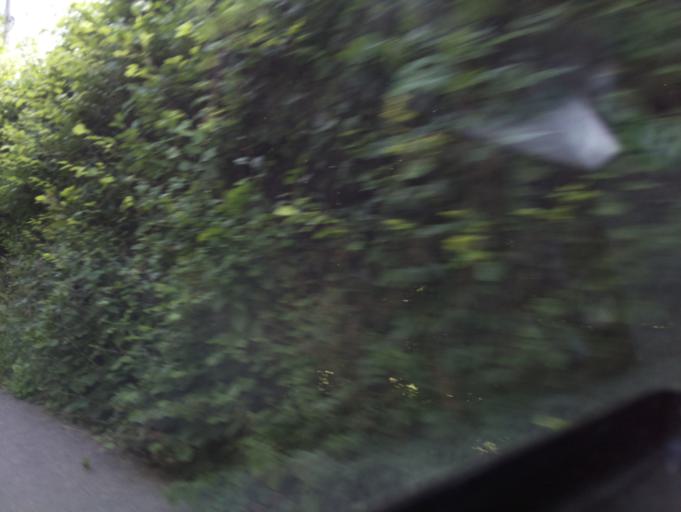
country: GB
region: England
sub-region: Gloucestershire
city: Cinderford
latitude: 51.8263
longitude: -2.4544
